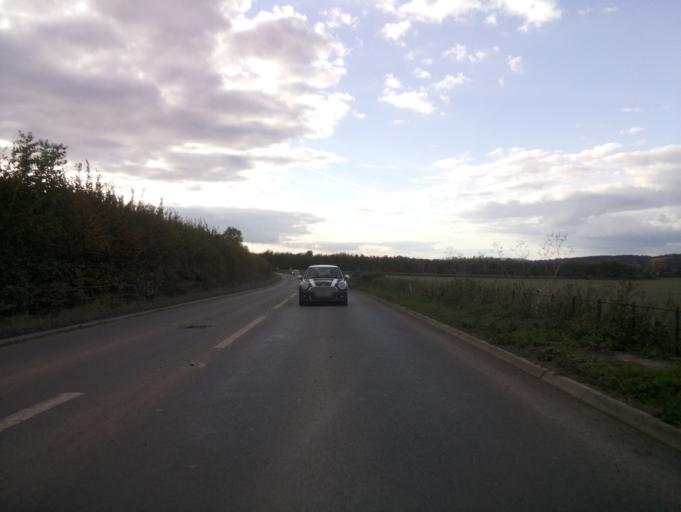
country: GB
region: England
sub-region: Herefordshire
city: Ocle Pychard
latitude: 52.0663
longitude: -2.5757
